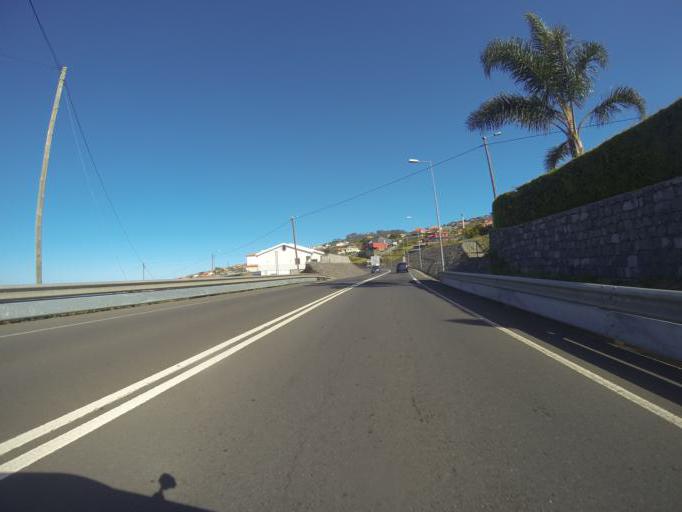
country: PT
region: Madeira
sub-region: Calheta
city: Estreito da Calheta
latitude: 32.7332
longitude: -17.1931
